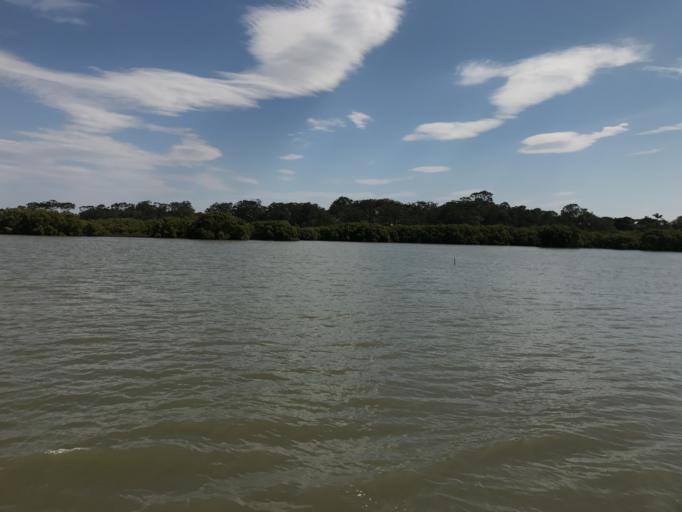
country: AU
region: Queensland
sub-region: Redland
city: Cleveland
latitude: -27.5297
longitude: 153.2861
